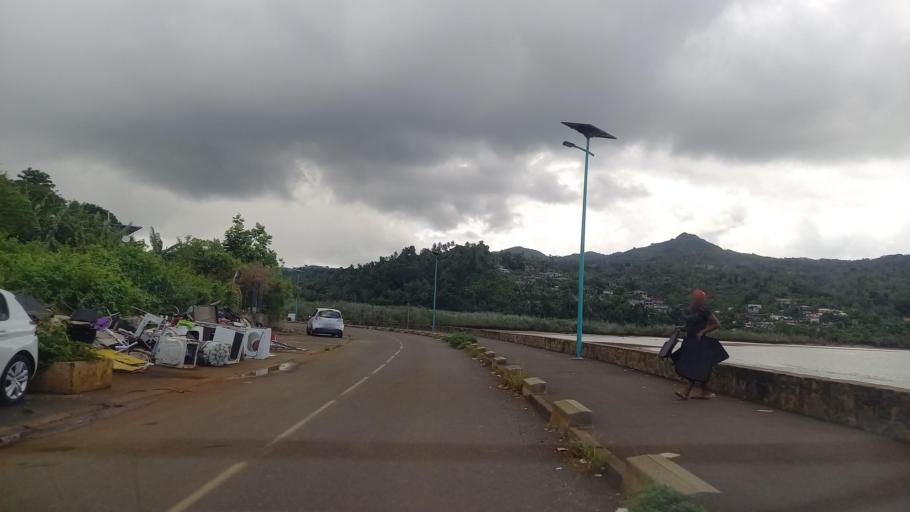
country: YT
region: Chiconi
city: Chiconi
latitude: -12.8376
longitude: 45.1135
